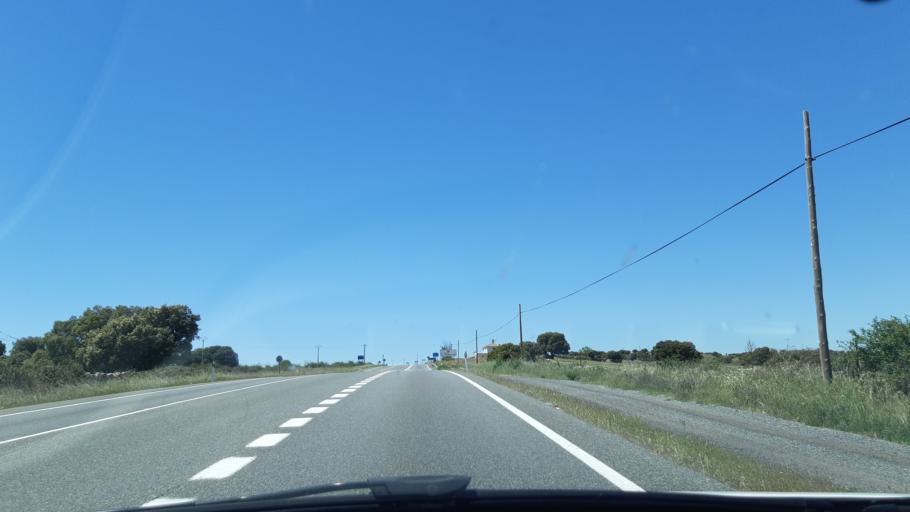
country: ES
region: Castille and Leon
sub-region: Provincia de Segovia
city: Zarzuela del Monte
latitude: 40.7598
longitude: -4.3375
